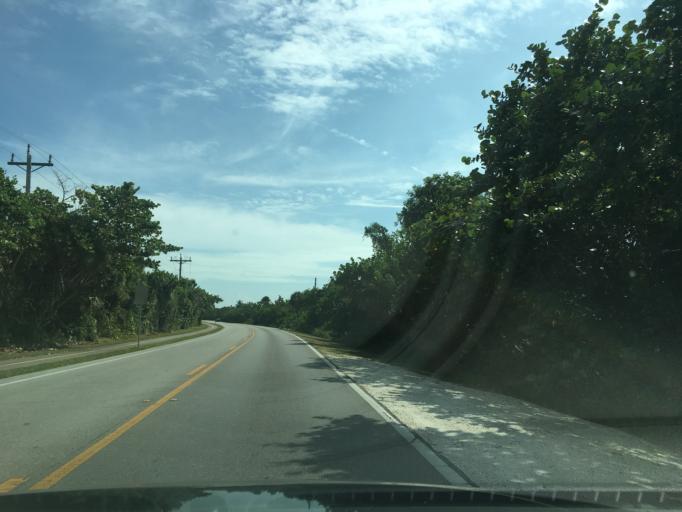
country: US
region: Florida
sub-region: Lee County
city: Saint James City
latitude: 26.4717
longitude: -82.1645
